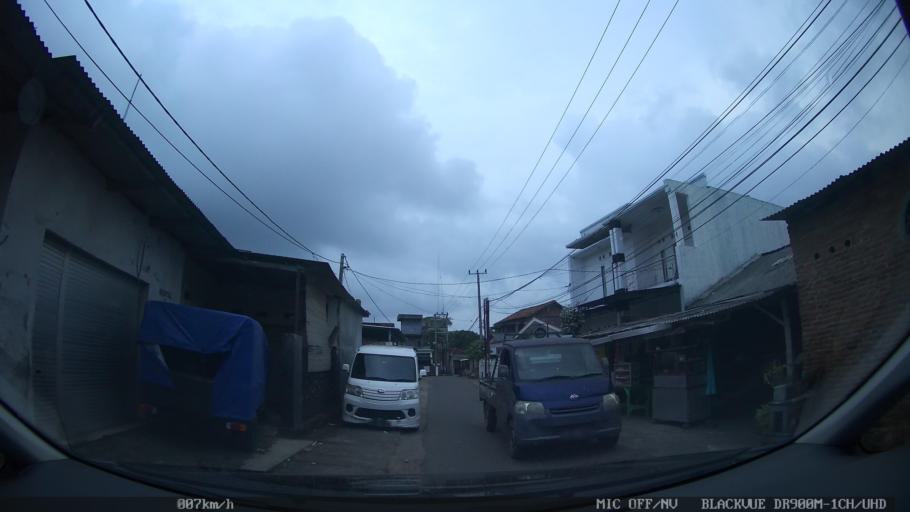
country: ID
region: Lampung
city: Bandarlampung
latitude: -5.4074
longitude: 105.2791
